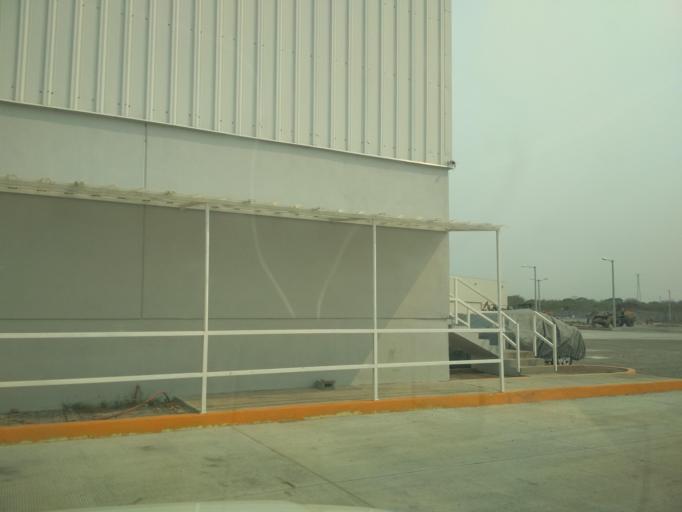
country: MX
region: Veracruz
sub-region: Veracruz
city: Delfino Victoria (Santa Fe)
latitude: 19.1646
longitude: -96.2657
